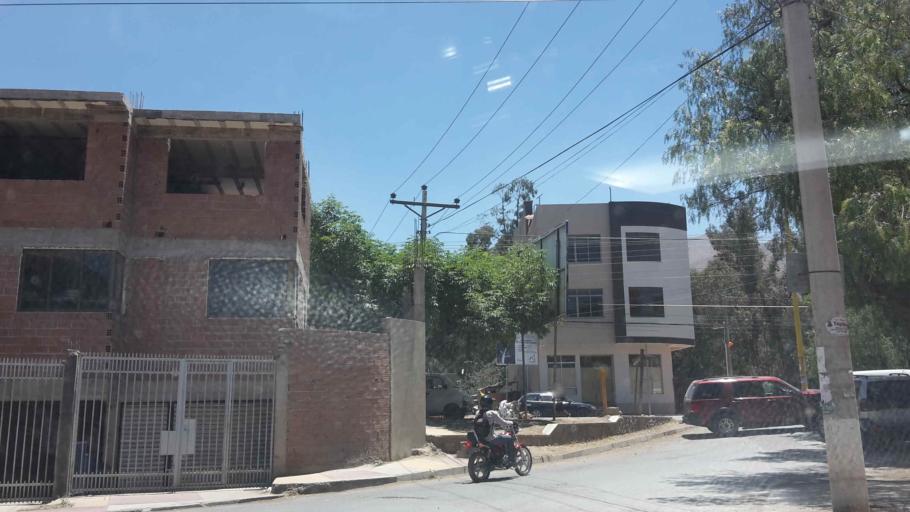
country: BO
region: Cochabamba
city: Cochabamba
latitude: -17.3417
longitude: -66.2140
